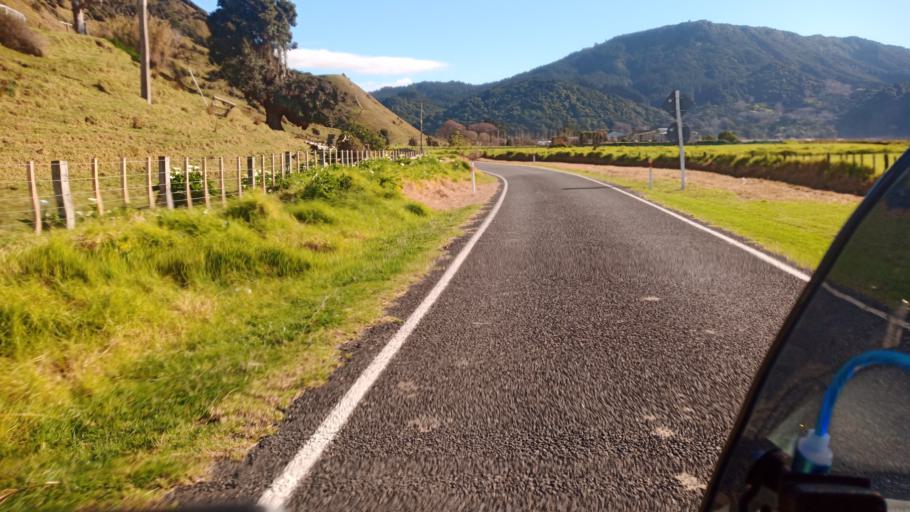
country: NZ
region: Gisborne
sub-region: Gisborne District
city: Gisborne
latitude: -38.2464
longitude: 178.3151
